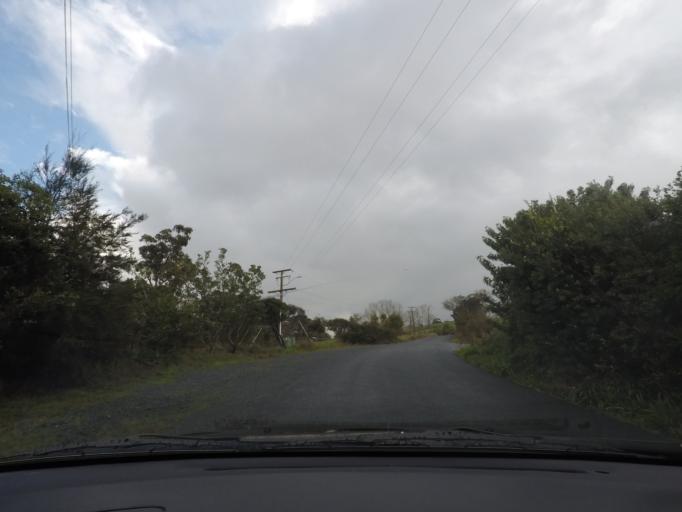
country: NZ
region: Auckland
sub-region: Auckland
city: Warkworth
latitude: -36.4319
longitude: 174.7313
